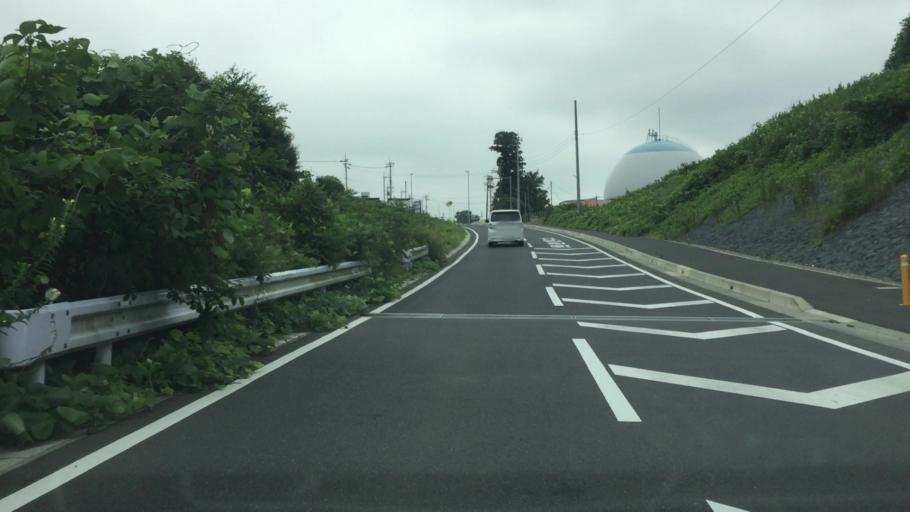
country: JP
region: Chiba
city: Abiko
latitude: 35.8366
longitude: 140.0168
